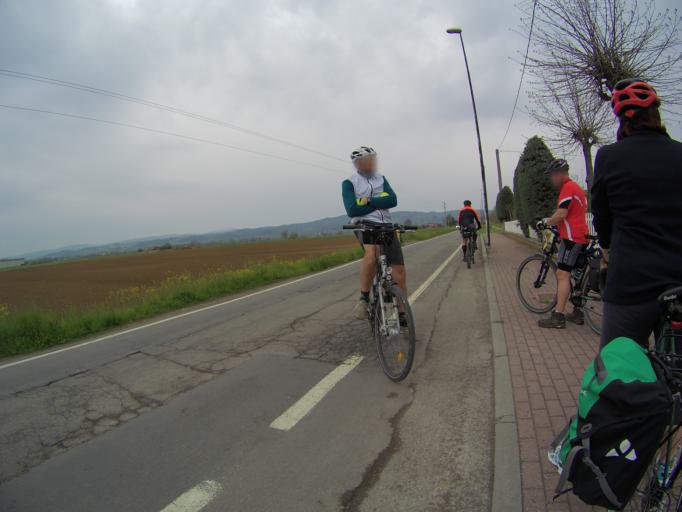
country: IT
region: Emilia-Romagna
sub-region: Provincia di Reggio Emilia
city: Bibbiano
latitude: 44.6630
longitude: 10.4988
